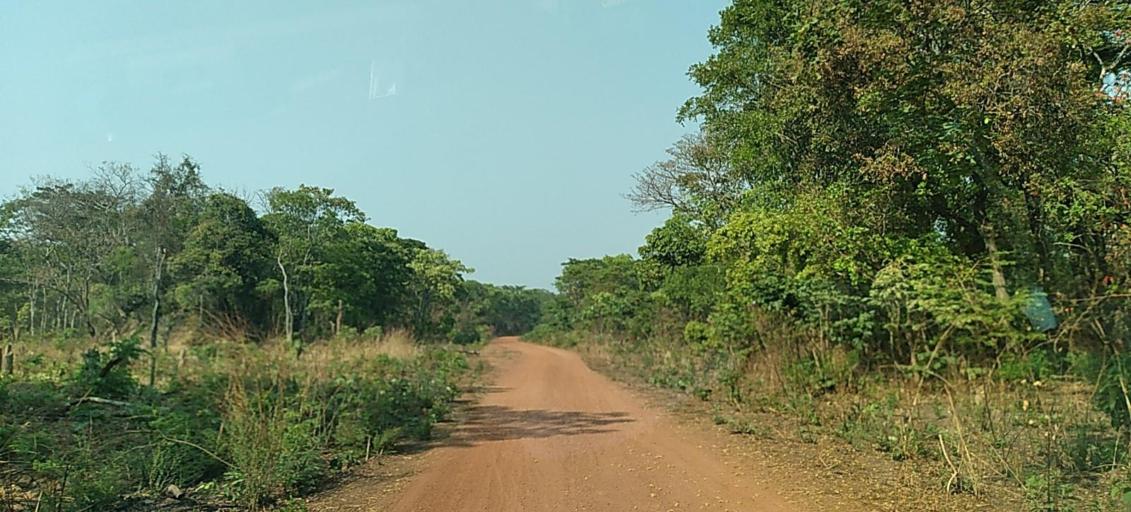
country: ZM
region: Copperbelt
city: Chingola
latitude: -12.8685
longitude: 27.4556
